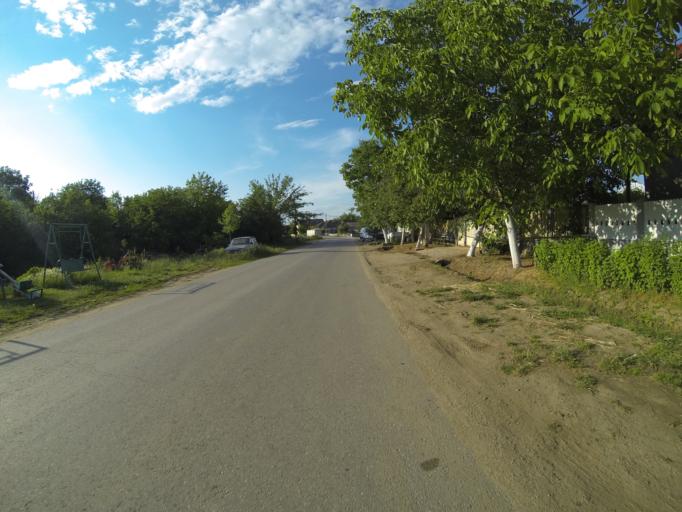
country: RO
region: Dolj
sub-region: Comuna Tuglui
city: Tuglui
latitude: 44.2018
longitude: 23.7993
